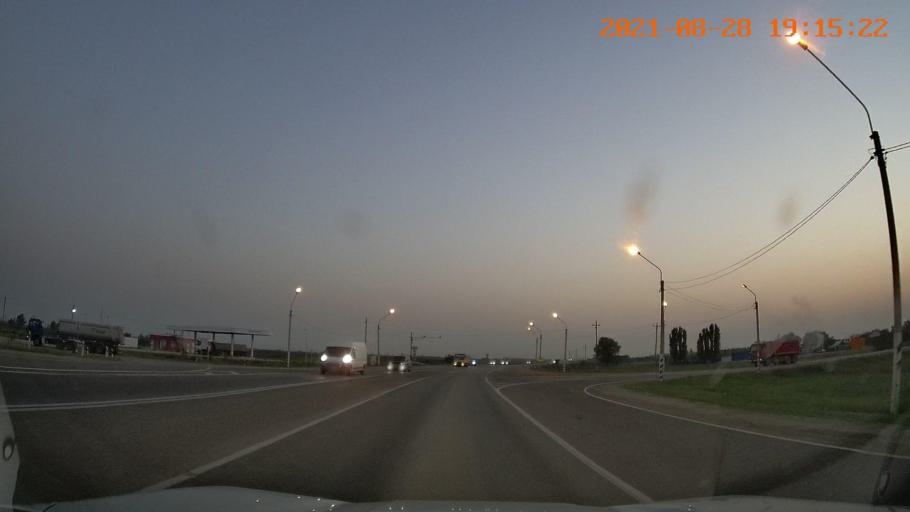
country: RU
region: Krasnodarskiy
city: Ryazanskaya
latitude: 44.9193
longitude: 39.5787
